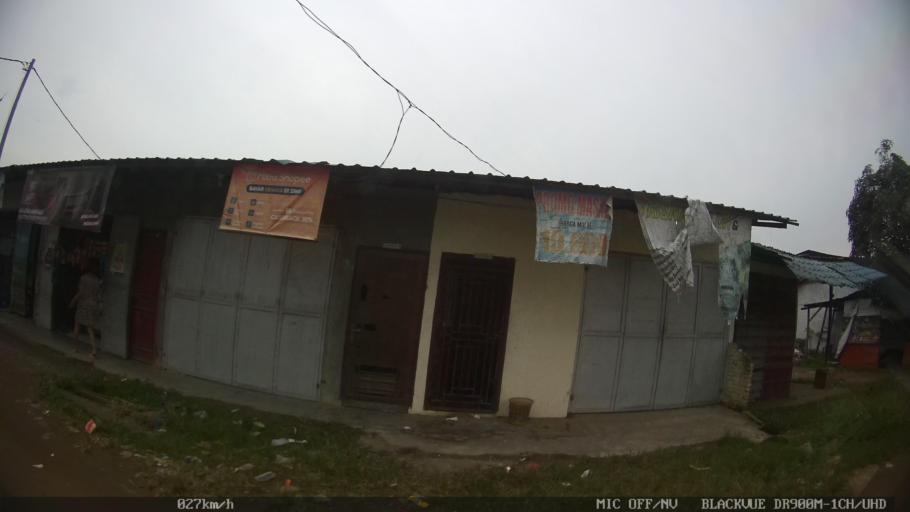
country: ID
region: North Sumatra
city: Deli Tua
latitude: 3.5488
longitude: 98.7280
